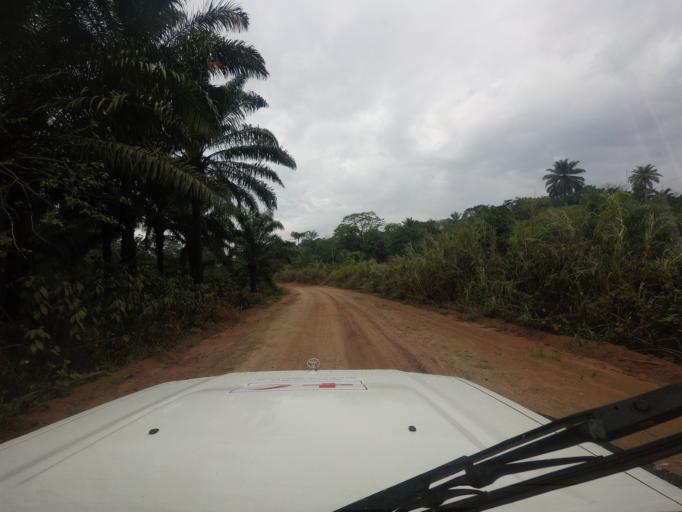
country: SL
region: Eastern Province
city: Buedu
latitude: 8.3436
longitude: -10.1723
